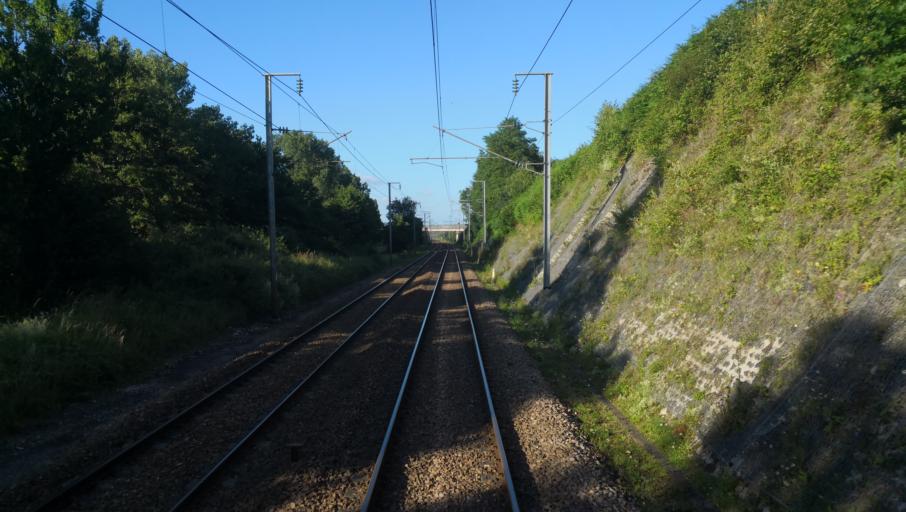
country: FR
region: Haute-Normandie
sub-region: Departement de l'Eure
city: Claville
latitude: 48.9796
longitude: 1.0161
